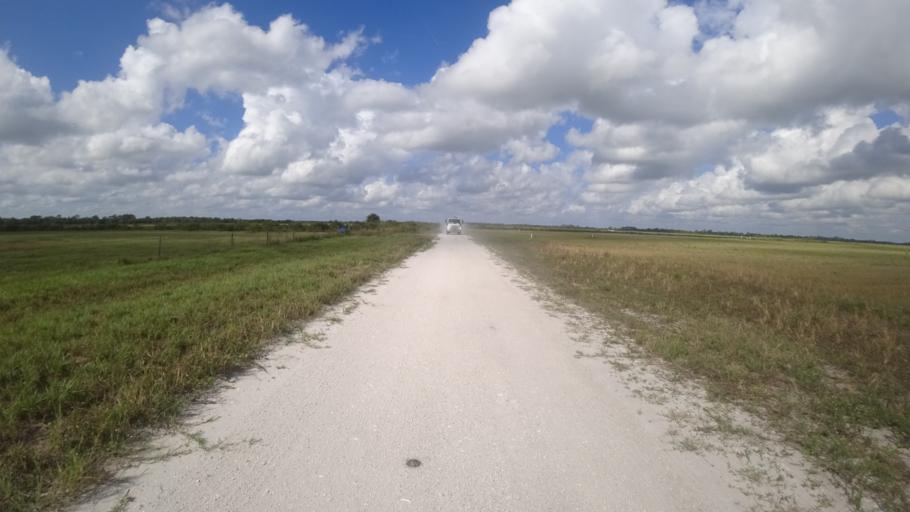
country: US
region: Florida
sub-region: Sarasota County
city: Lake Sarasota
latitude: 27.4034
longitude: -82.2020
